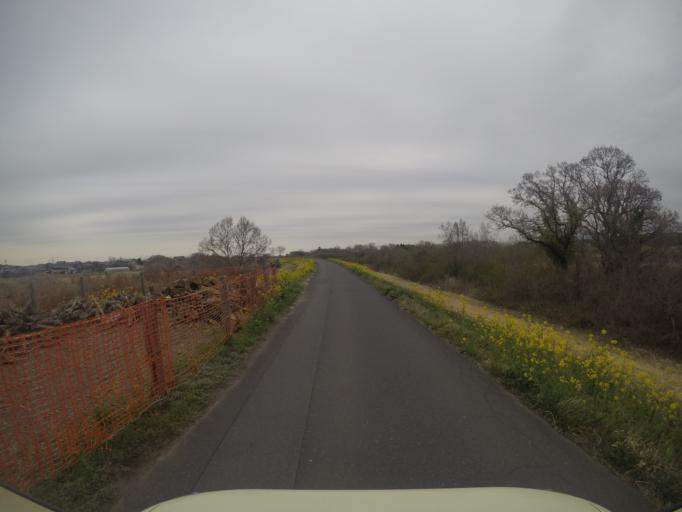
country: JP
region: Ibaraki
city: Ishige
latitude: 36.0810
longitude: 140.0026
